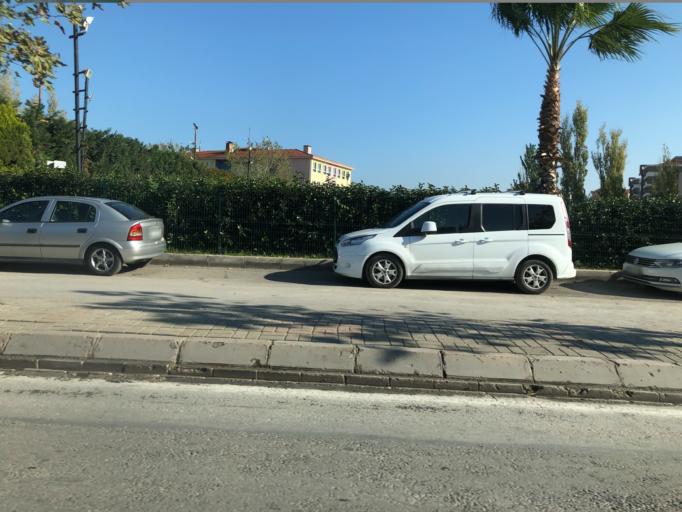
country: TR
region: Izmir
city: Izmir
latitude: 38.4563
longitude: 27.1764
